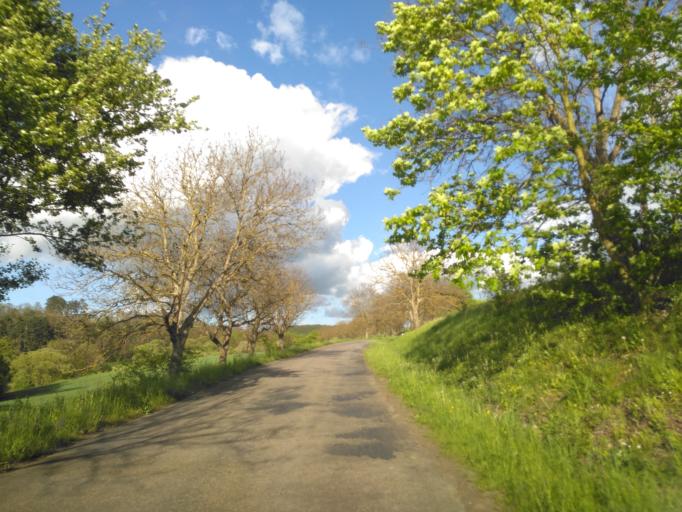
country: CZ
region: Central Bohemia
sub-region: Okres Beroun
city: Kraluv Dvur
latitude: 49.9221
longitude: 14.0530
